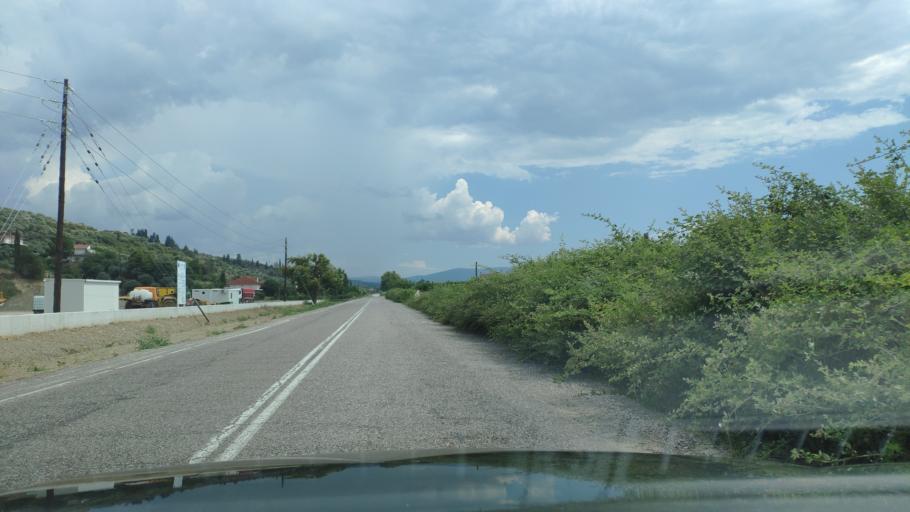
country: GR
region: West Greece
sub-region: Nomos Aitolias kai Akarnanias
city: Krikellos
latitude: 38.9635
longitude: 21.1703
